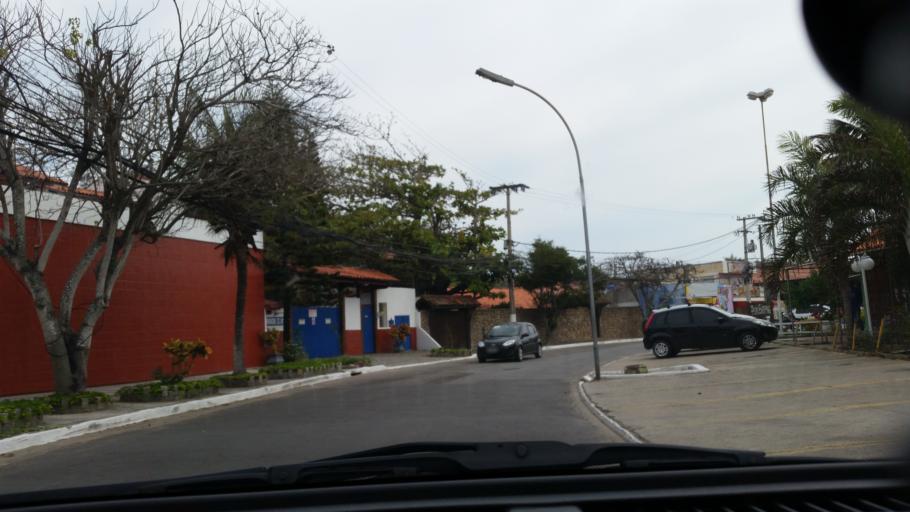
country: BR
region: Rio de Janeiro
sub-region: Cabo Frio
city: Cabo Frio
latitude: -22.8641
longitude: -41.9883
